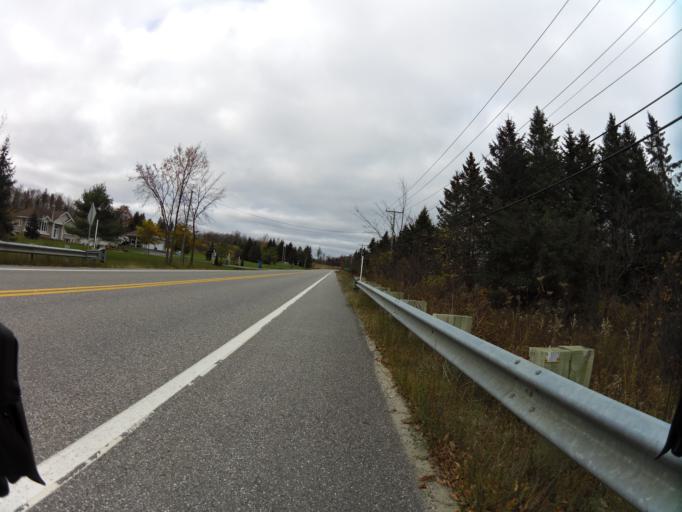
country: CA
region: Quebec
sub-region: Outaouais
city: Wakefield
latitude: 45.5816
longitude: -75.8837
